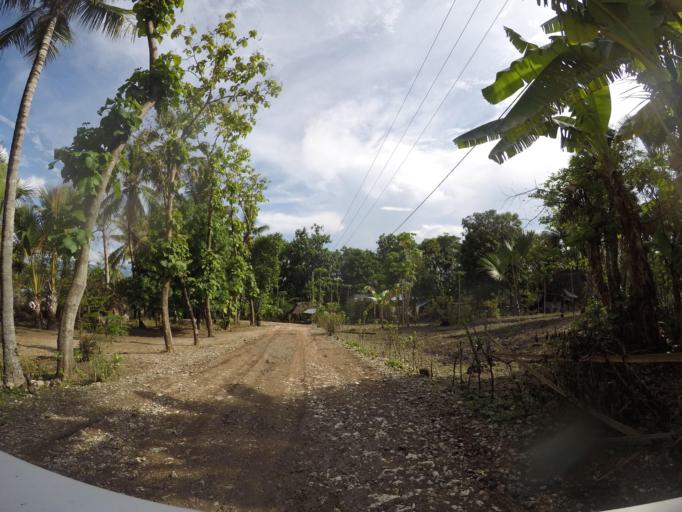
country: TL
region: Baucau
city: Baucau
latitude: -8.5022
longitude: 126.4620
